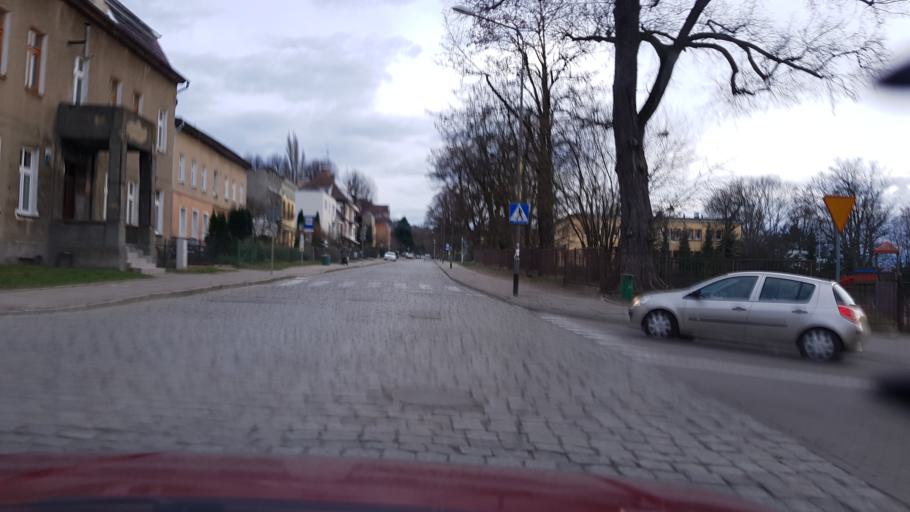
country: PL
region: West Pomeranian Voivodeship
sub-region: Szczecin
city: Szczecin
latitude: 53.3647
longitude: 14.5981
